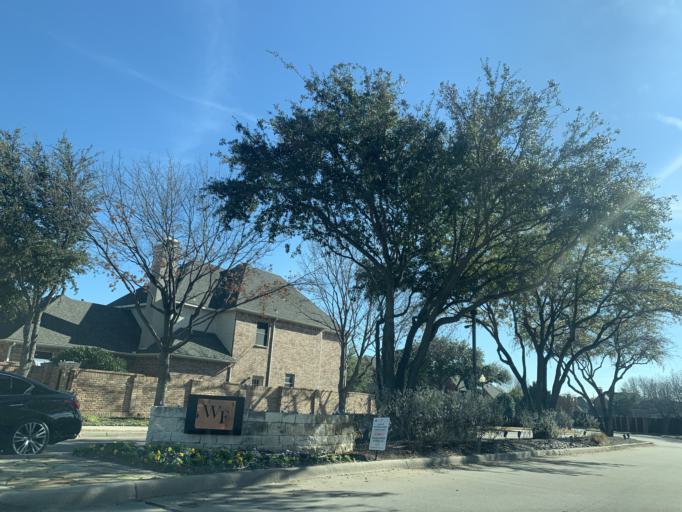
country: US
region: Texas
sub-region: Denton County
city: The Colony
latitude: 33.0566
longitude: -96.8191
